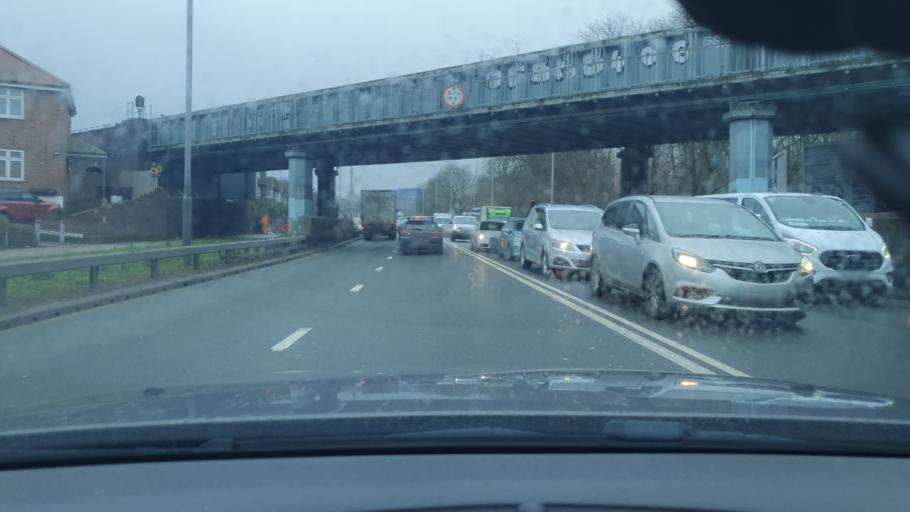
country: GB
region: England
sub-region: Greater London
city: Wood Green
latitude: 51.6131
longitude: -0.1325
